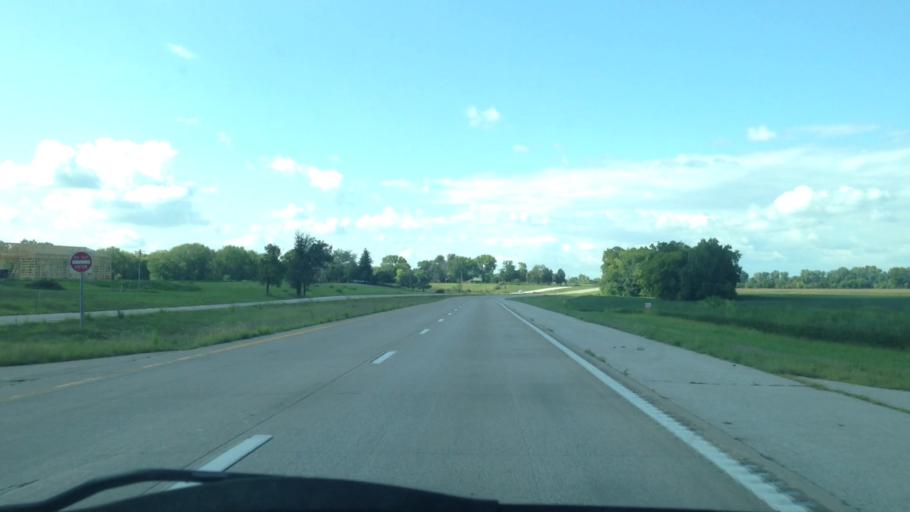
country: US
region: Missouri
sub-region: Lewis County
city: Canton
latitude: 40.2437
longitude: -91.5379
